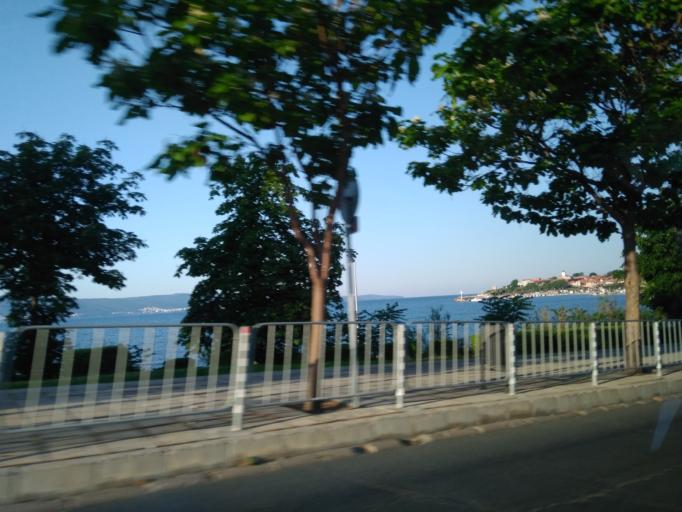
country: BG
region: Burgas
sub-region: Obshtina Nesebur
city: Nesebar
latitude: 42.6599
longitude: 27.7250
